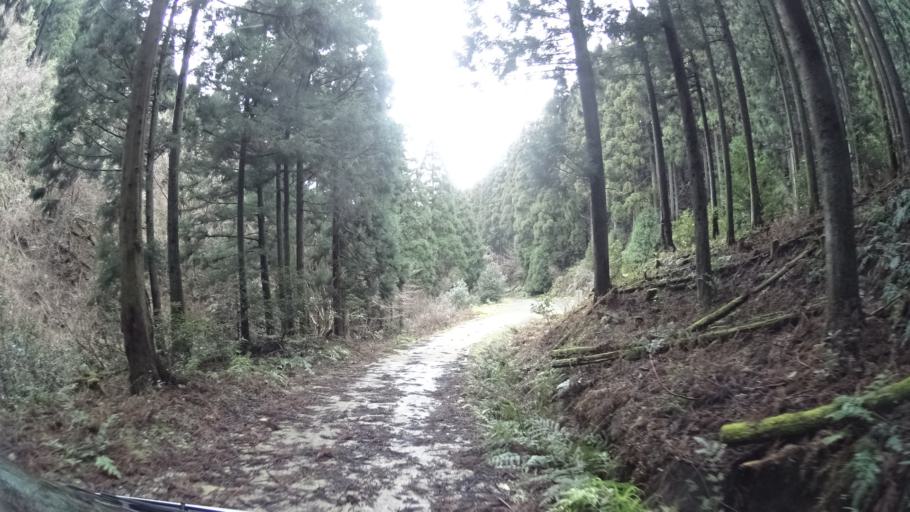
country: JP
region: Kyoto
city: Ayabe
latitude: 35.3092
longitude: 135.3772
